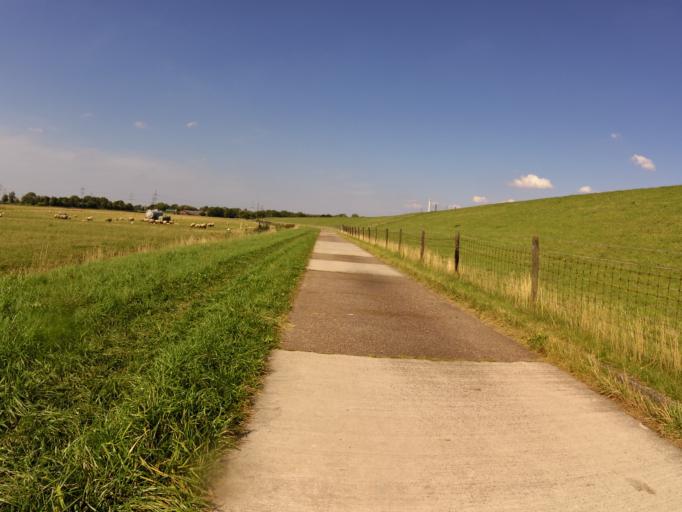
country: DE
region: Lower Saxony
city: Nordenham
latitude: 53.4179
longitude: 8.4724
